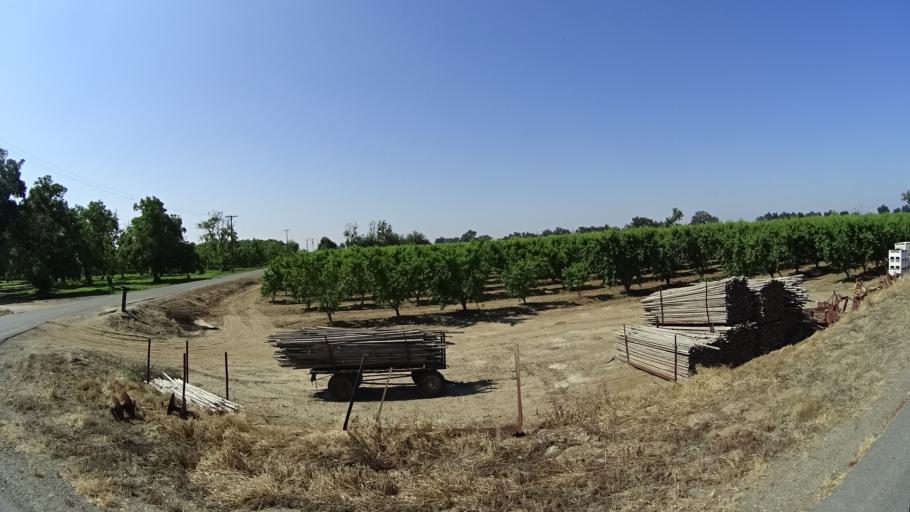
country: US
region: California
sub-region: Fresno County
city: Kingsburg
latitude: 36.4488
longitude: -119.5631
